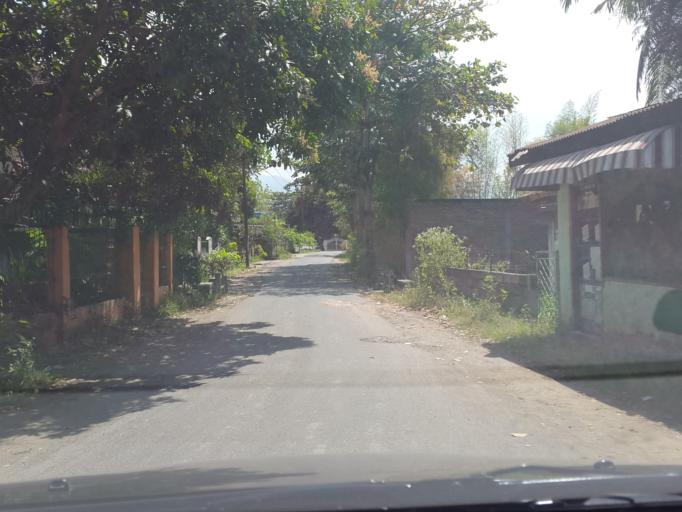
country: ID
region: West Nusa Tenggara
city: Kekeri
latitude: -8.5587
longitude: 116.1253
